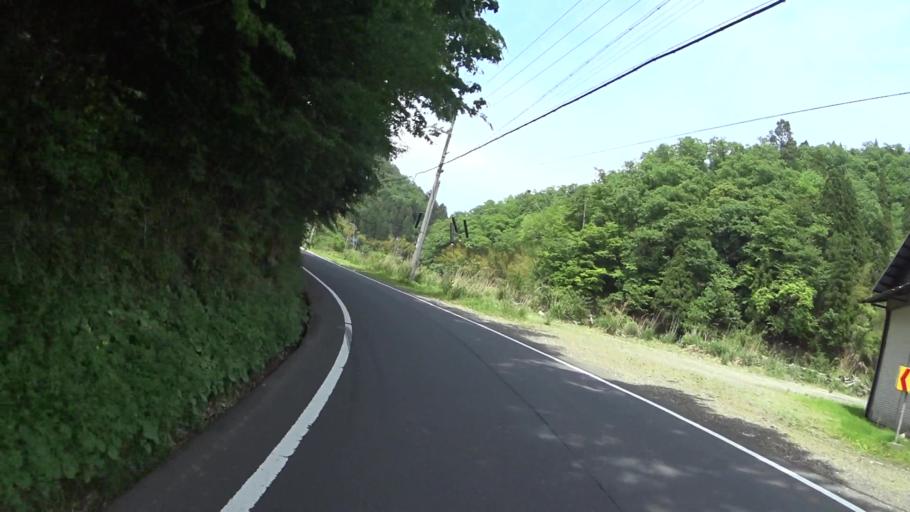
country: JP
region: Kyoto
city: Maizuru
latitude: 35.4315
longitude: 135.4788
